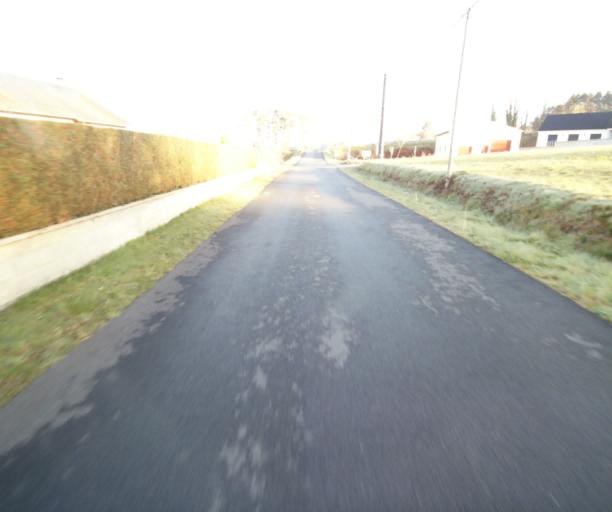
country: FR
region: Limousin
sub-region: Departement de la Correze
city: Correze
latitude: 45.3174
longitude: 1.8420
